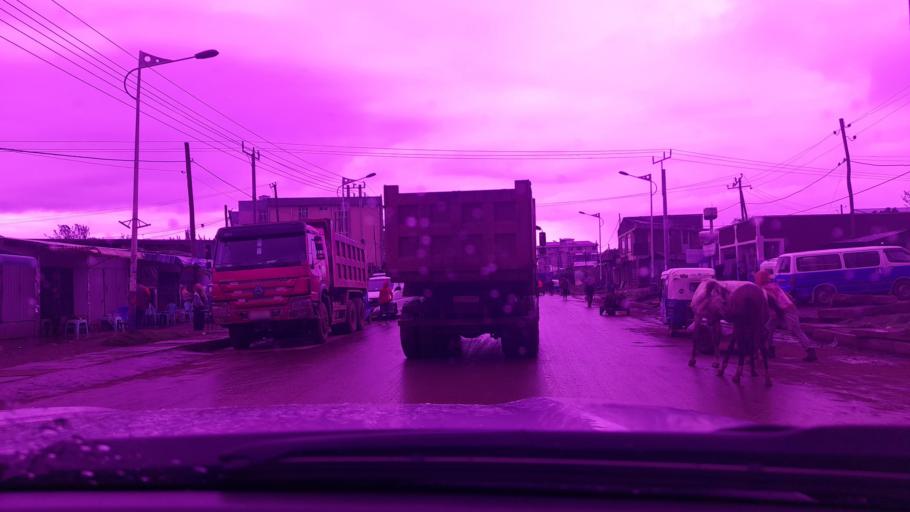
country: ET
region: Oromiya
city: Jima
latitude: 7.6673
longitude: 36.8425
